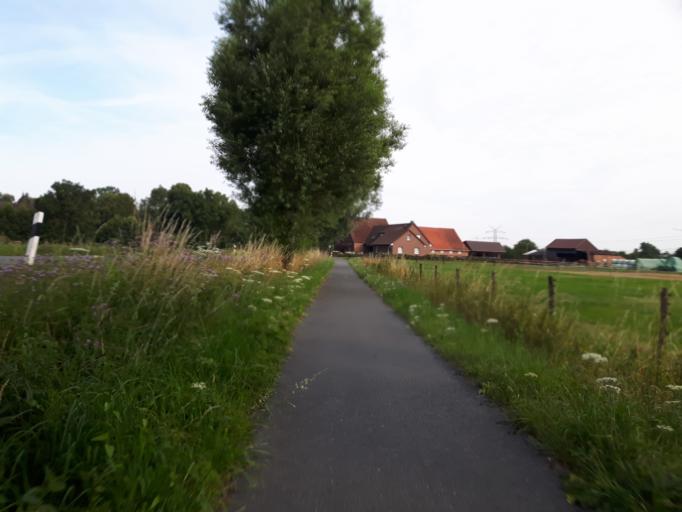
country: DE
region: Lower Saxony
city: Delmenhorst
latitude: 53.0997
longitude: 8.5756
